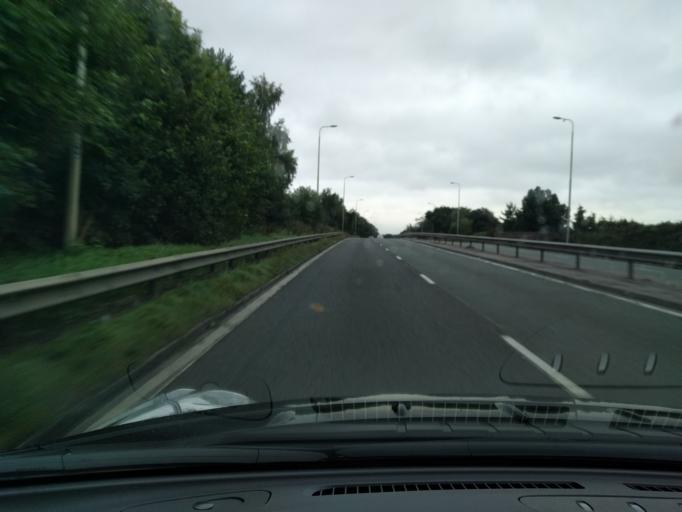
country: GB
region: England
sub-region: Borough of Wigan
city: Ashton in Makerfield
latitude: 53.4724
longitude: -2.6485
